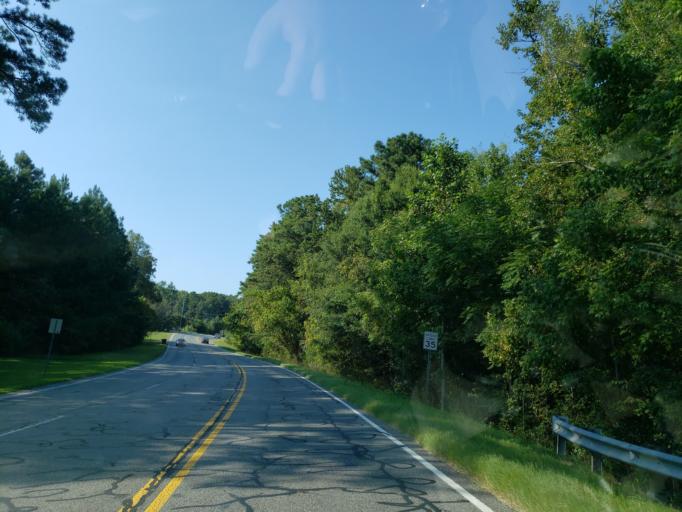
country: US
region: Georgia
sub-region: Whitfield County
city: Varnell
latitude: 34.8956
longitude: -84.9751
